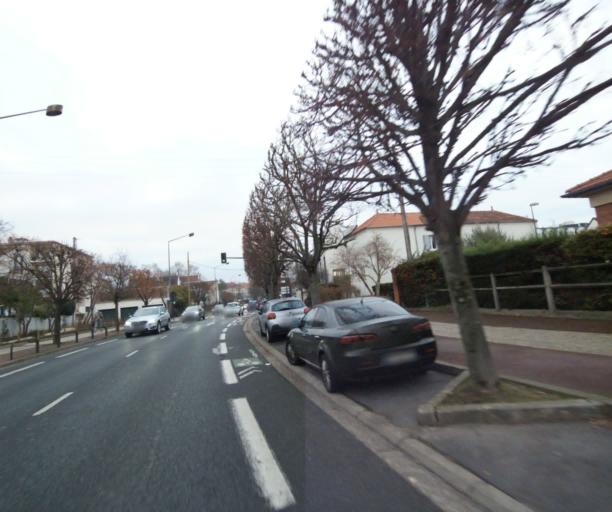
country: FR
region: Ile-de-France
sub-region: Departement des Hauts-de-Seine
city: Rueil-Malmaison
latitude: 48.8823
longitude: 2.1832
